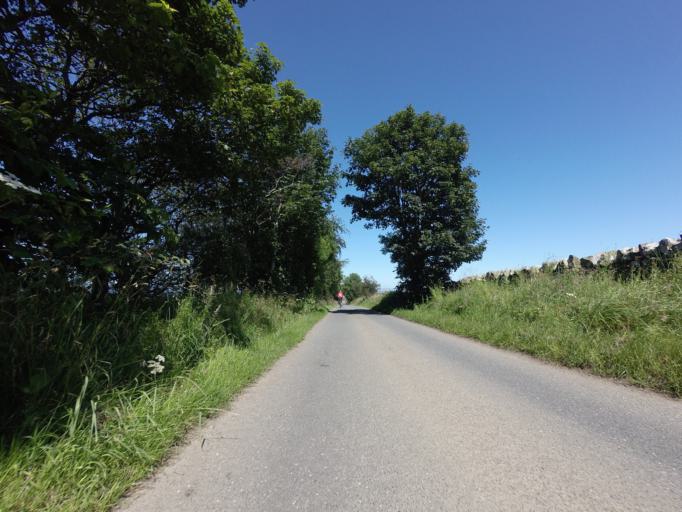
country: GB
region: Scotland
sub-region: Aberdeenshire
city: Macduff
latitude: 57.6510
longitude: -2.5032
